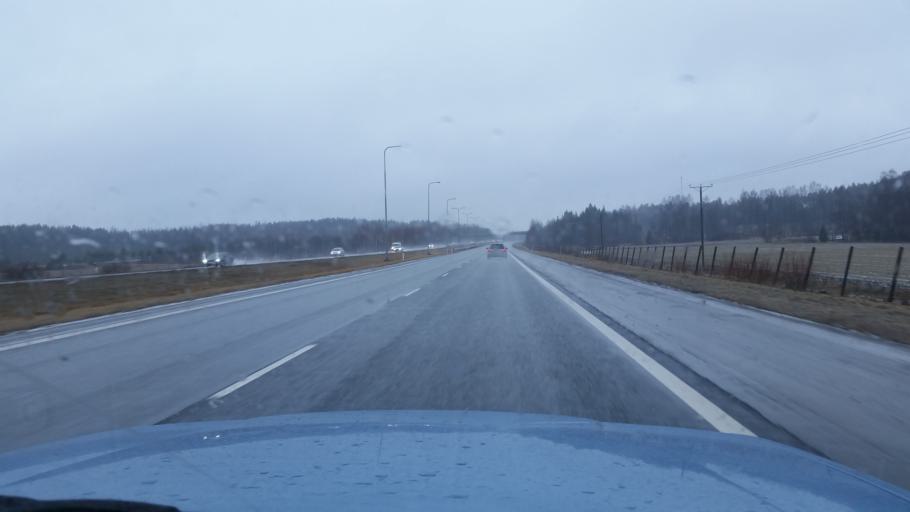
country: FI
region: Haeme
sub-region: Haemeenlinna
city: Tervakoski
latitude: 60.8489
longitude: 24.6129
